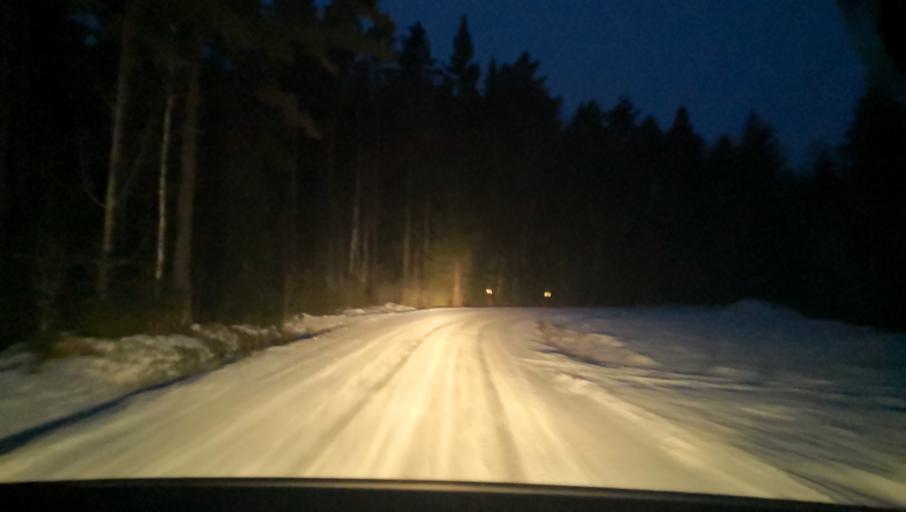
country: SE
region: Uppsala
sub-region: Heby Kommun
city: Tarnsjo
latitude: 60.2581
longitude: 16.7742
